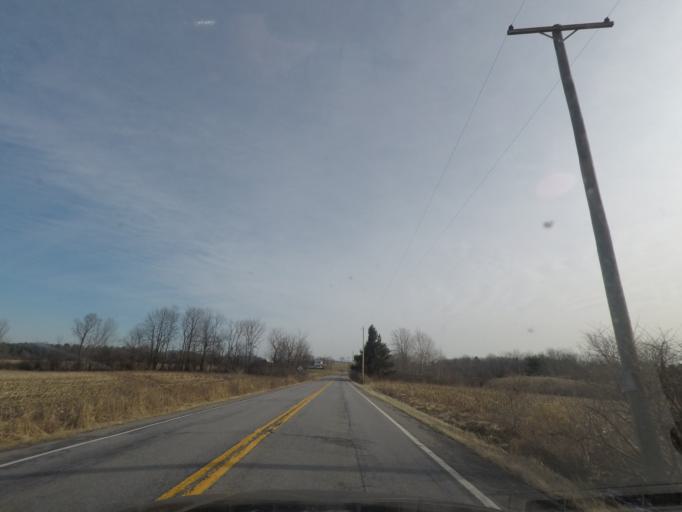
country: US
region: New York
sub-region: Saratoga County
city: Stillwater
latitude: 42.9866
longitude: -73.6596
